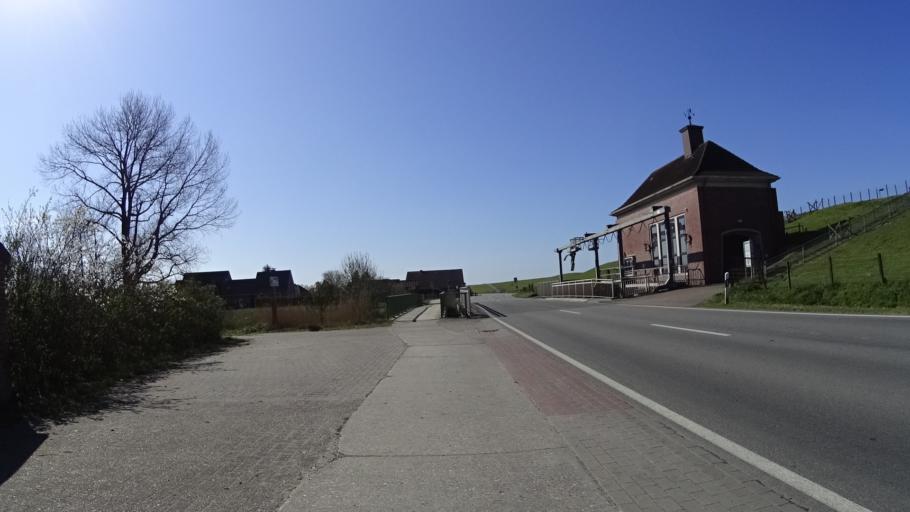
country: DE
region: Lower Saxony
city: Jemgum
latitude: 53.2545
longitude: 7.4059
